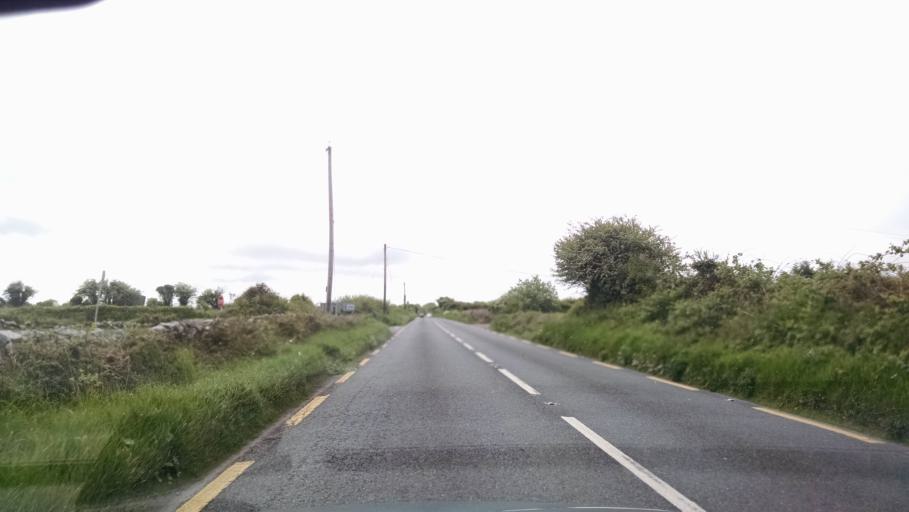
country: IE
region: Connaught
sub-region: County Galway
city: Claregalway
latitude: 53.3712
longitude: -9.0166
